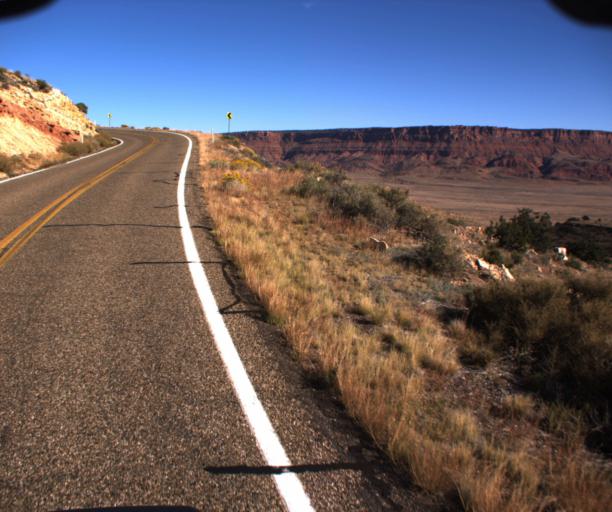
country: US
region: Arizona
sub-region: Coconino County
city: Fredonia
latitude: 36.7245
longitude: -112.0648
